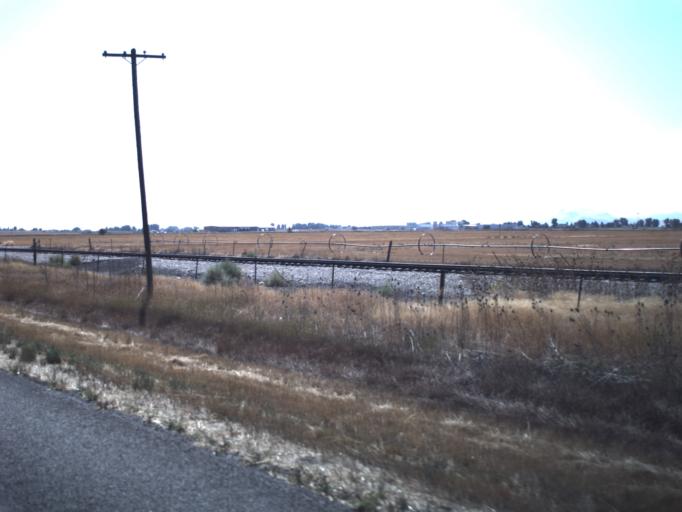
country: US
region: Utah
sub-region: Cache County
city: Lewiston
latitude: 41.9843
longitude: -111.8129
